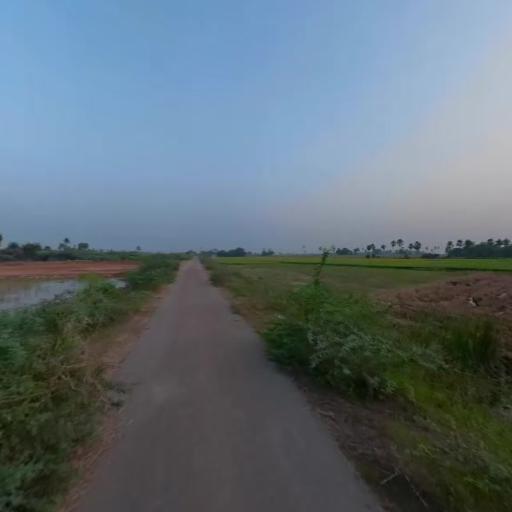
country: IN
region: Telangana
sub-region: Nalgonda
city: Suriapet
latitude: 17.0676
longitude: 79.5480
